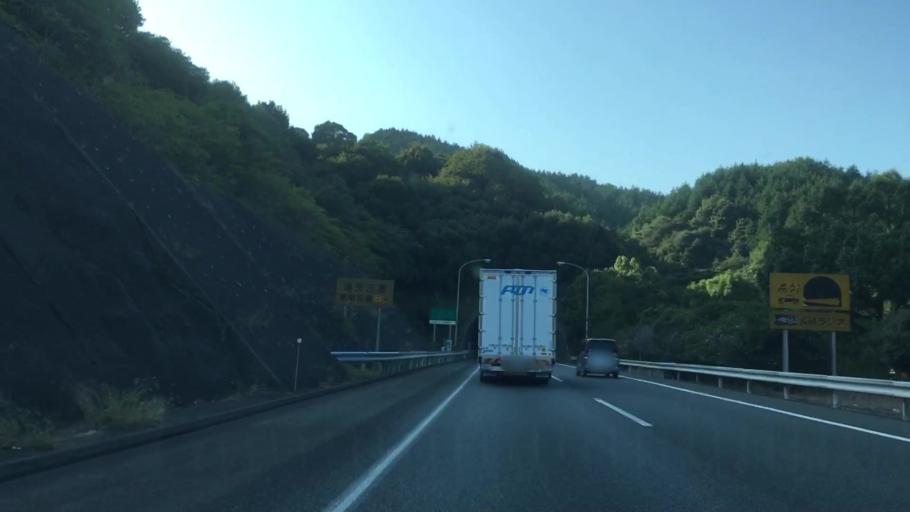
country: JP
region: Yamaguchi
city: Hofu
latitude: 34.0785
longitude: 131.4876
